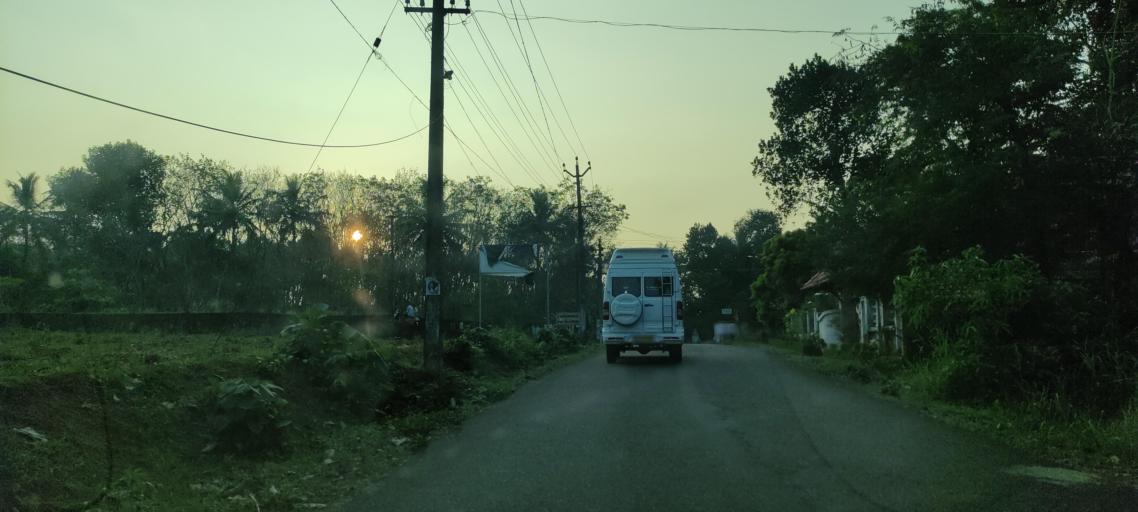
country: IN
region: Kerala
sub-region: Alappuzha
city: Kattanam
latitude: 9.1439
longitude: 76.5682
